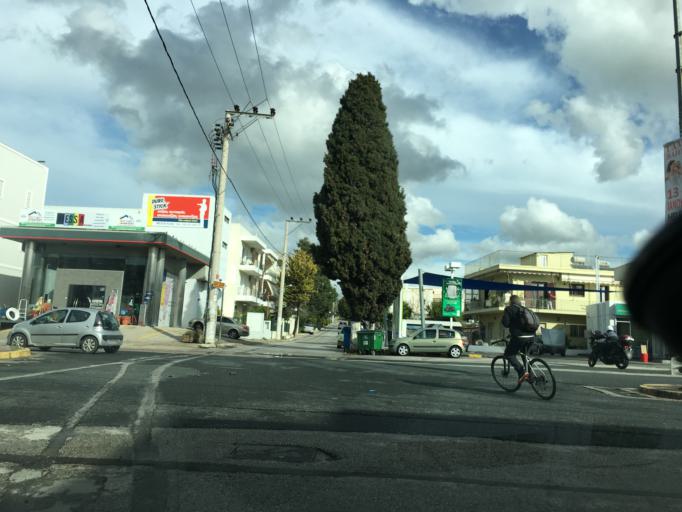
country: GR
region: Attica
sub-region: Nomarchia Athinas
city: Irakleio
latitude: 38.0412
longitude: 23.7754
